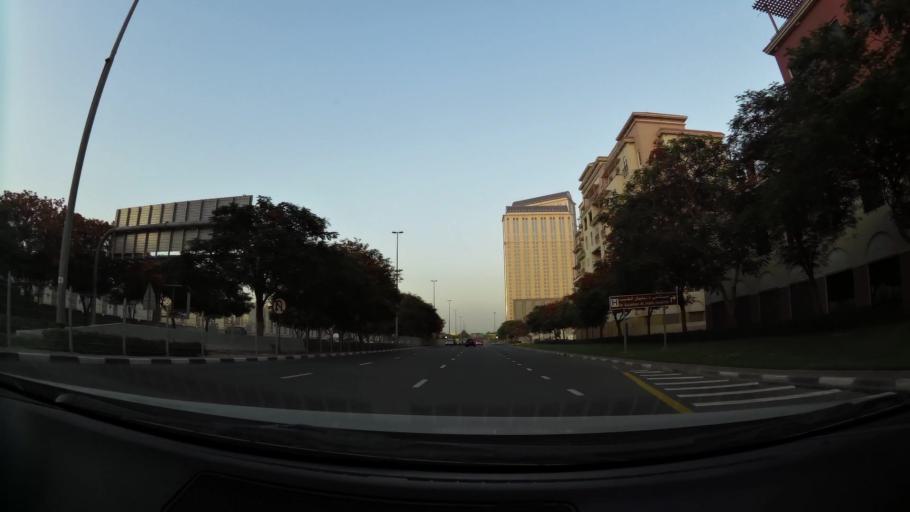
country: AE
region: Ash Shariqah
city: Sharjah
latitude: 25.2346
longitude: 55.3192
